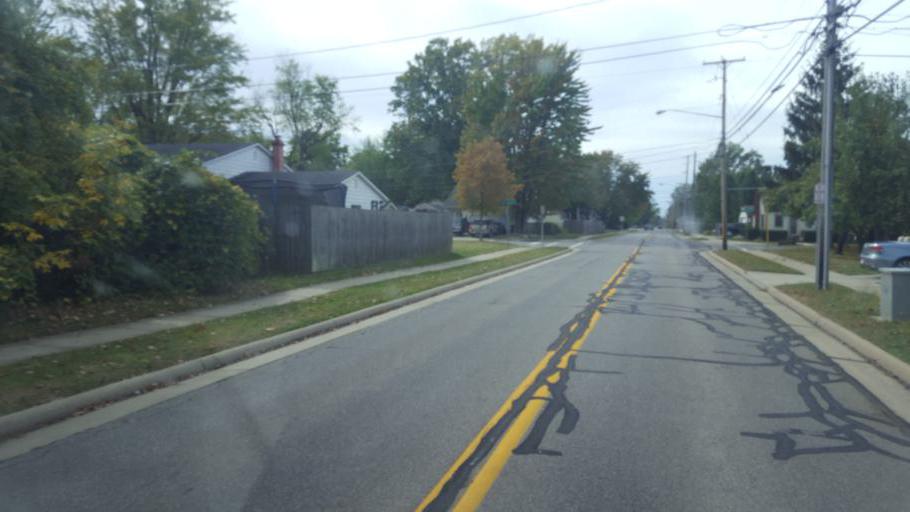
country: US
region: Ohio
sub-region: Lorain County
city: Sheffield Lake
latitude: 41.4850
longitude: -82.1015
